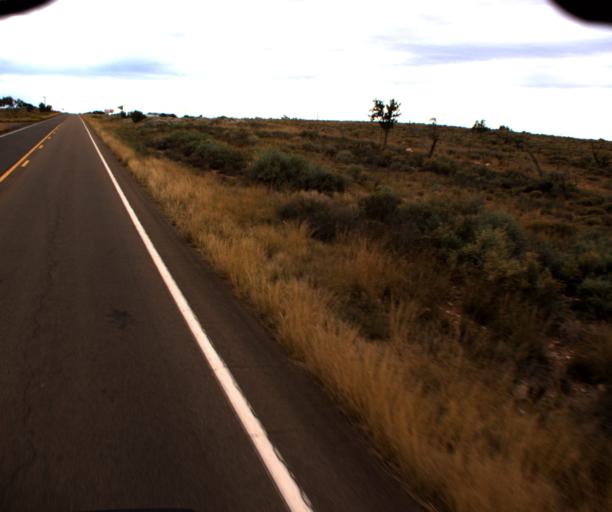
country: US
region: Arizona
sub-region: Navajo County
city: Snowflake
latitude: 34.5690
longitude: -110.0825
